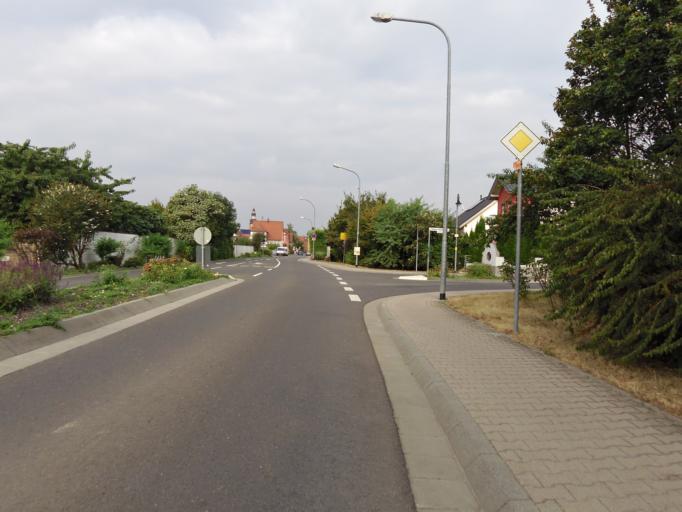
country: DE
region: Rheinland-Pfalz
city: Grossniedesheim
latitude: 49.5744
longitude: 8.3181
